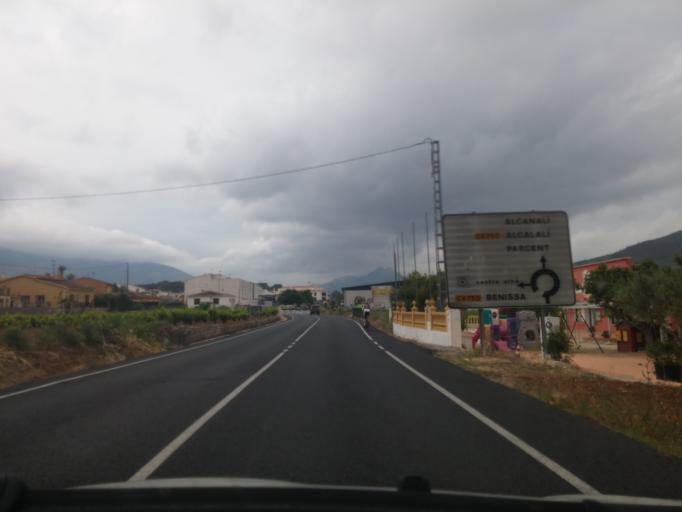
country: ES
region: Valencia
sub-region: Provincia de Alicante
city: Jalon
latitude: 38.7417
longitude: -0.0056
